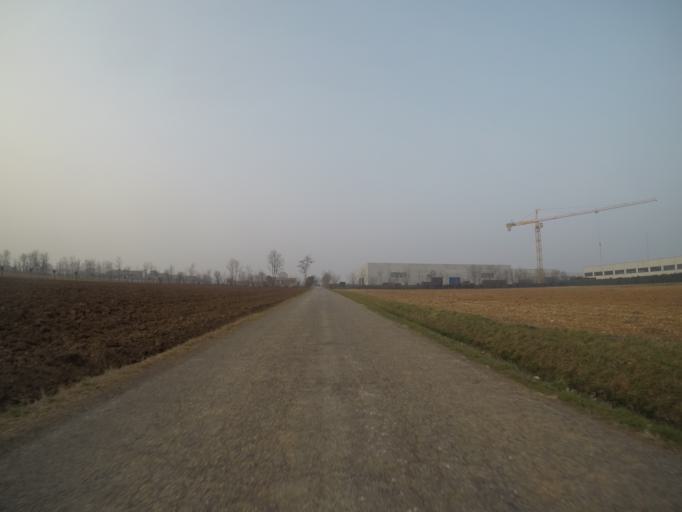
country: IT
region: Veneto
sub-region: Provincia di Treviso
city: Altivole
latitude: 45.7376
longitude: 11.9608
